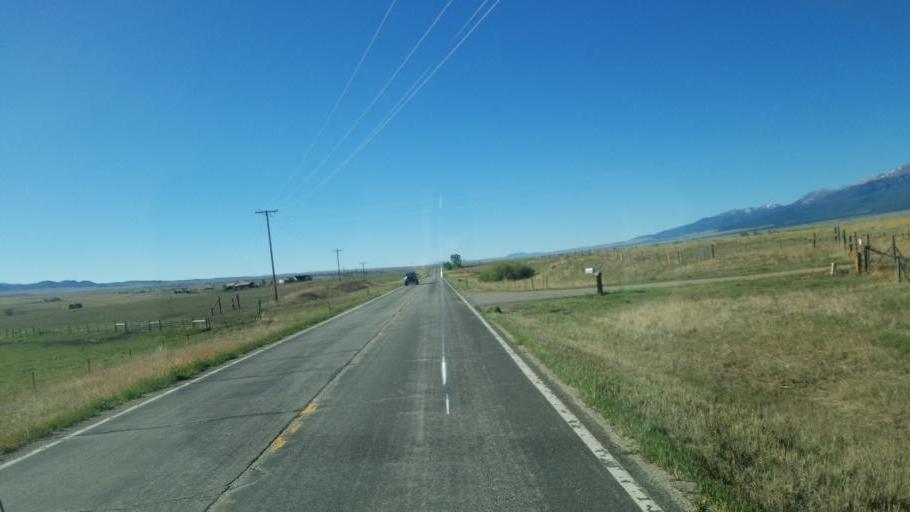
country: US
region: Colorado
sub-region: Custer County
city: Westcliffe
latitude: 38.1796
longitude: -105.5080
